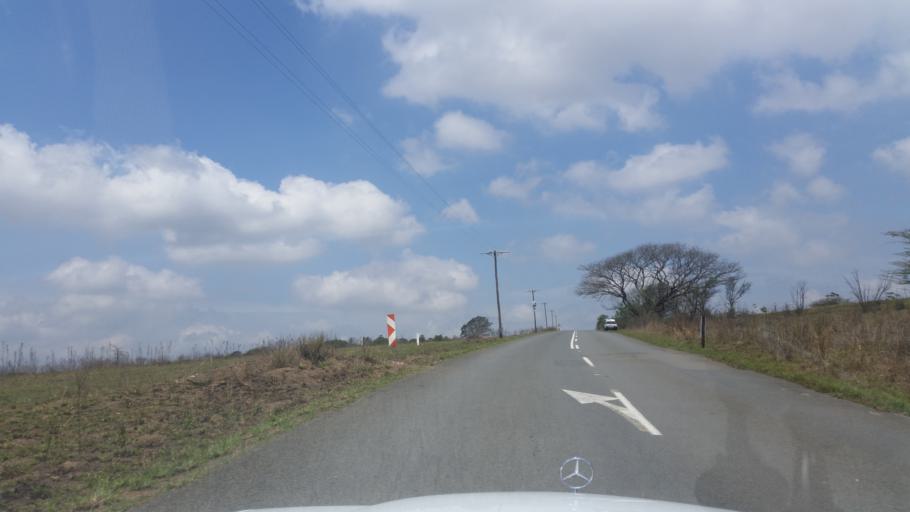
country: ZA
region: KwaZulu-Natal
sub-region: uMgungundlovu District Municipality
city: Camperdown
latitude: -29.7054
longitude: 30.4952
